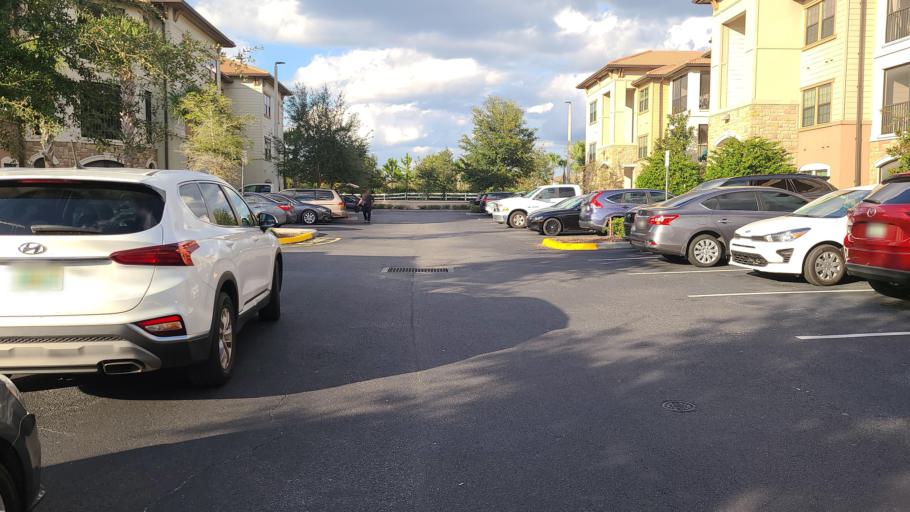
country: US
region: Florida
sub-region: Osceola County
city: Buenaventura Lakes
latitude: 28.3581
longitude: -81.2378
